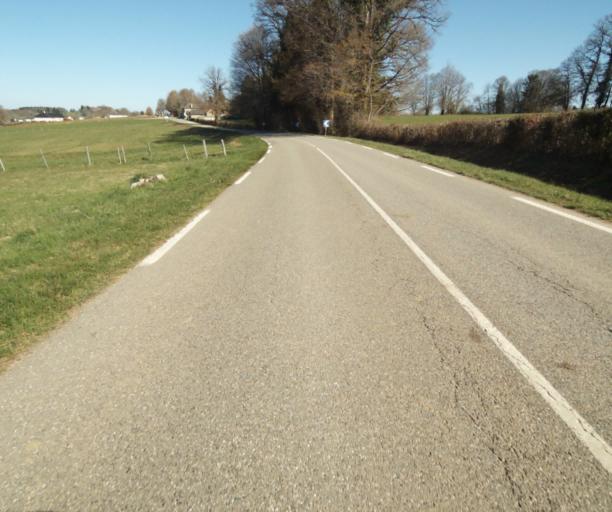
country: FR
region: Limousin
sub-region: Departement de la Correze
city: Seilhac
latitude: 45.3681
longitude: 1.7260
